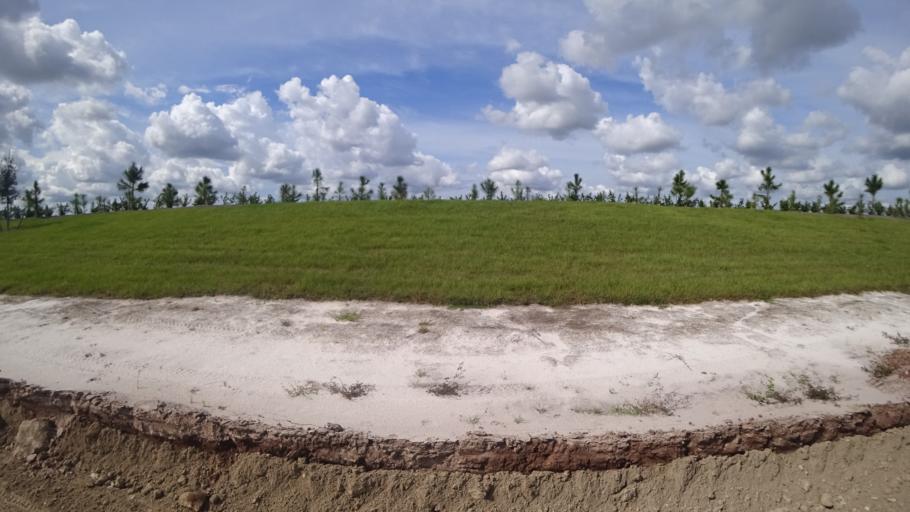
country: US
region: Florida
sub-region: Sarasota County
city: The Meadows
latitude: 27.4325
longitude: -82.3522
